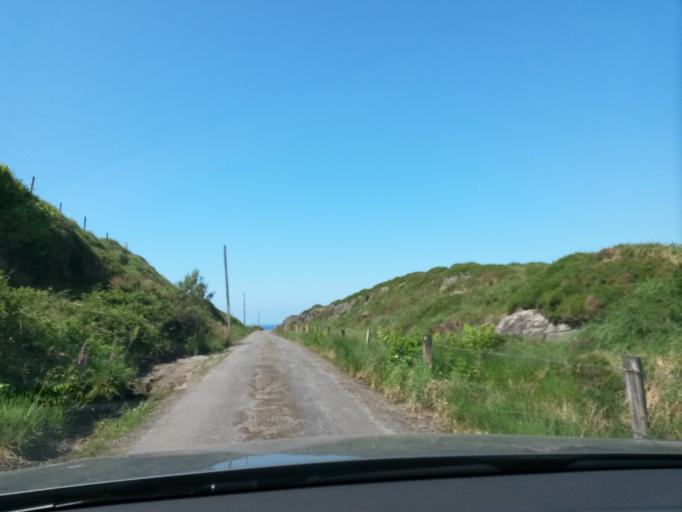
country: IE
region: Munster
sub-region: Ciarrai
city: Cahersiveen
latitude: 51.7299
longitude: -9.9736
